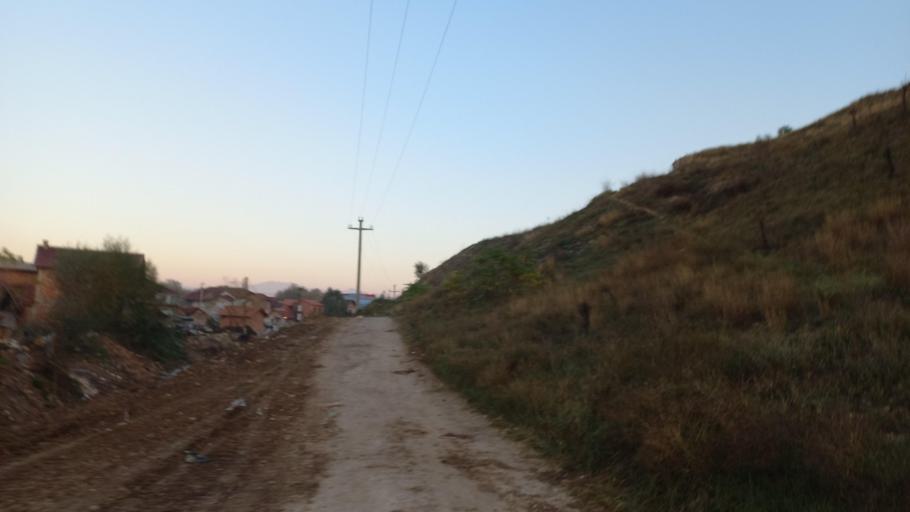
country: MK
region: Kumanovo
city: Kumanovo
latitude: 42.1405
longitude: 21.7252
